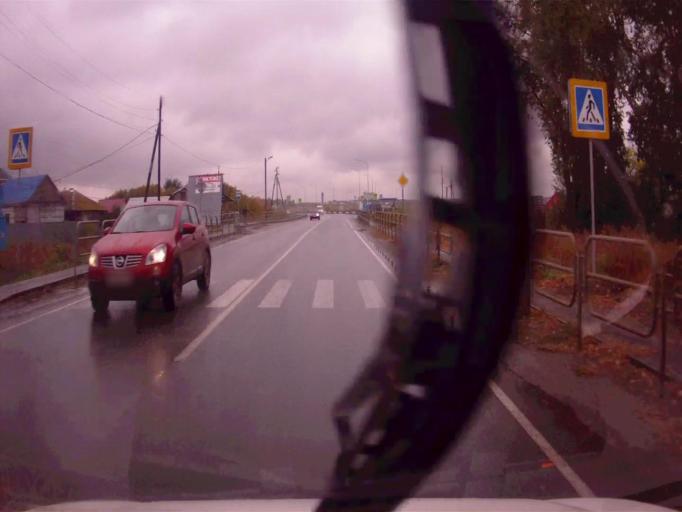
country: RU
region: Chelyabinsk
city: Roshchino
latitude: 55.3683
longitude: 61.1866
